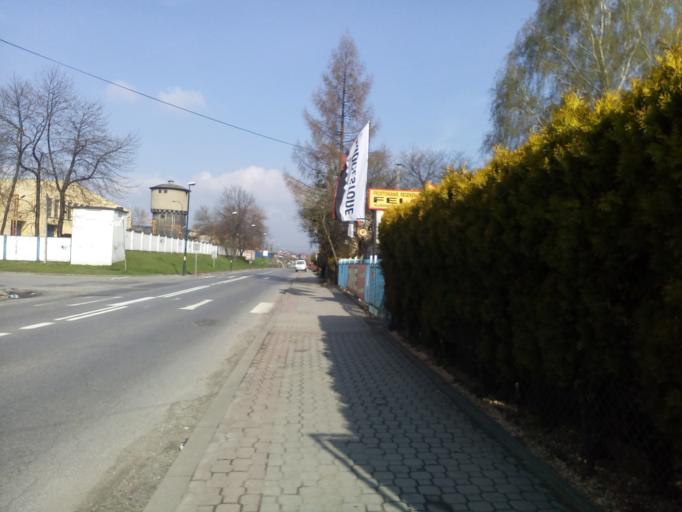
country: PL
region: Lesser Poland Voivodeship
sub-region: Powiat nowosadecki
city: Nowy Sacz
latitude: 49.6059
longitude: 20.7119
